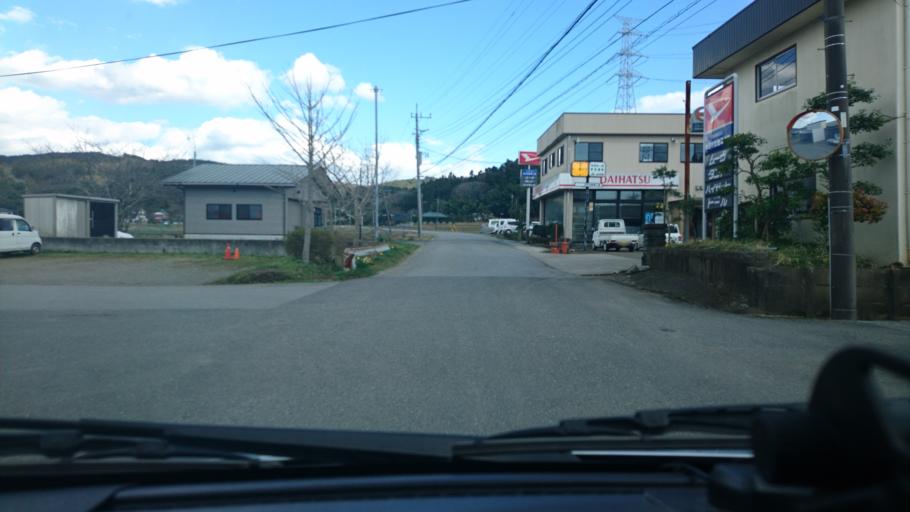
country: JP
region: Chiba
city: Kimitsu
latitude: 35.2869
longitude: 139.9881
